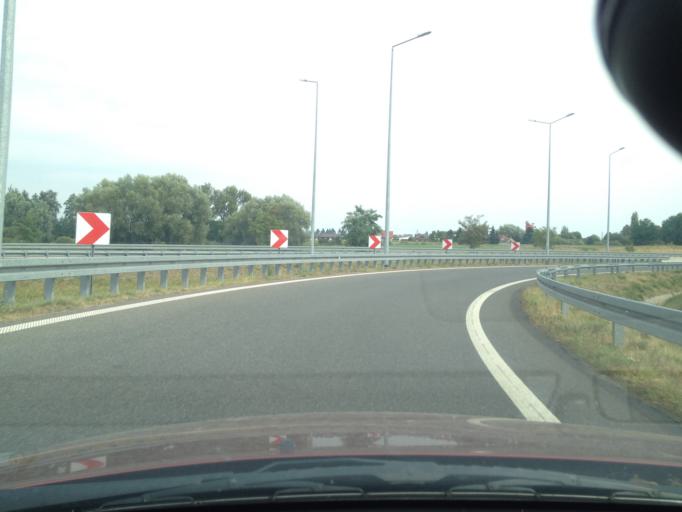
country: PL
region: West Pomeranian Voivodeship
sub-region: Powiat pyrzycki
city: Lipiany
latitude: 52.9530
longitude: 14.9475
